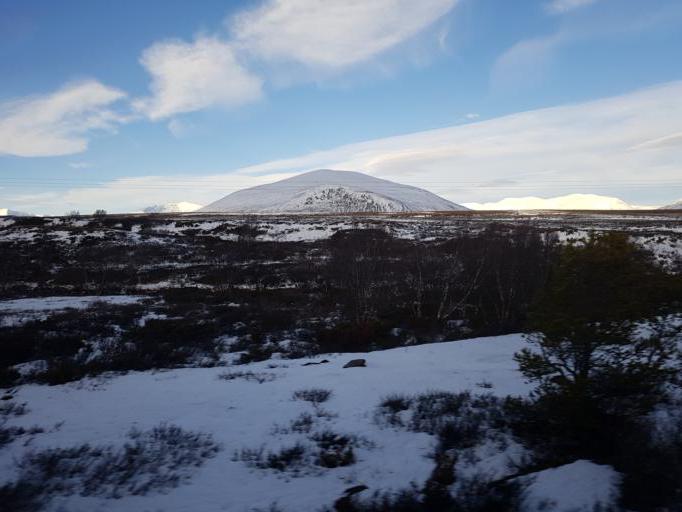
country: NO
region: Sor-Trondelag
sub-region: Oppdal
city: Oppdal
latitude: 62.2704
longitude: 9.5824
